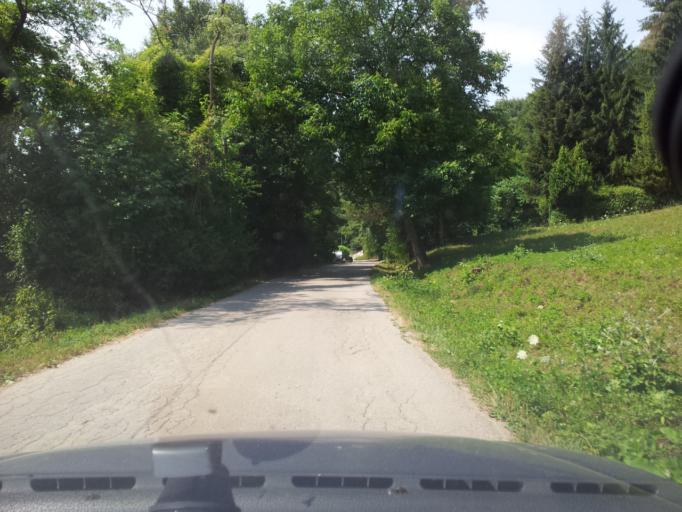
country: SK
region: Trenciansky
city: Nova Dubnica
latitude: 48.9075
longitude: 18.1110
